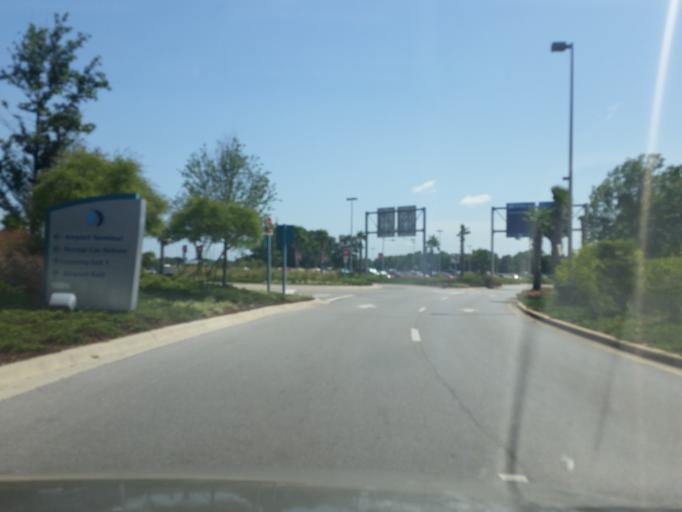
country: US
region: Florida
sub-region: Escambia County
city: Ferry Pass
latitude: 30.4752
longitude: -87.1967
